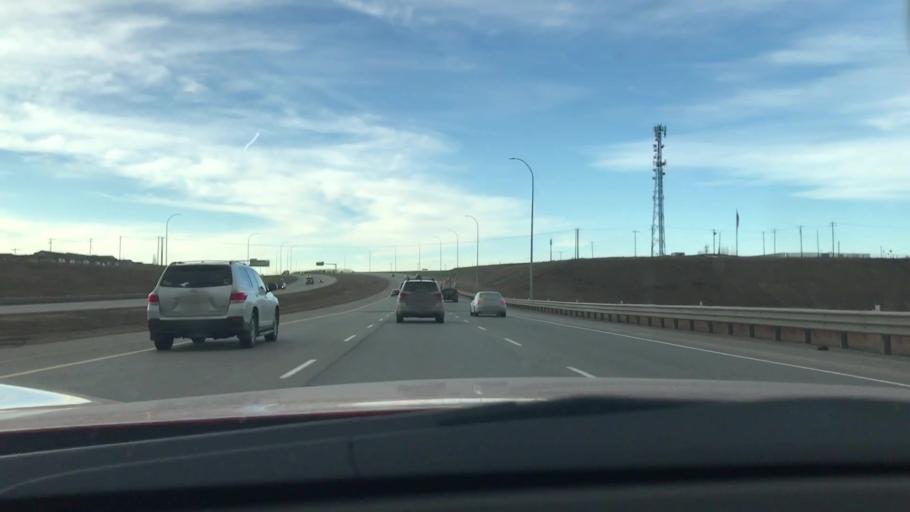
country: CA
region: Alberta
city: Calgary
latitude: 51.1510
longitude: -114.1838
